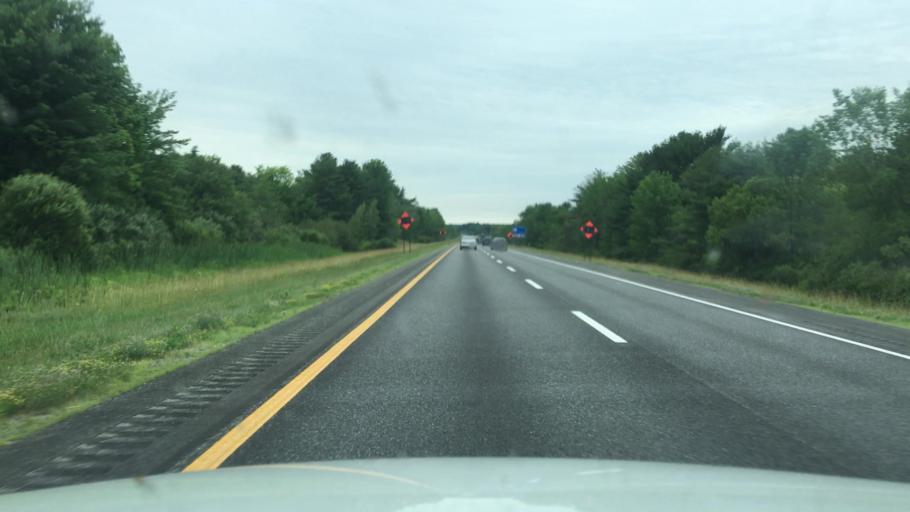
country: US
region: Maine
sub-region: Sagadahoc County
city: Richmond
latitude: 44.1135
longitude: -69.8584
